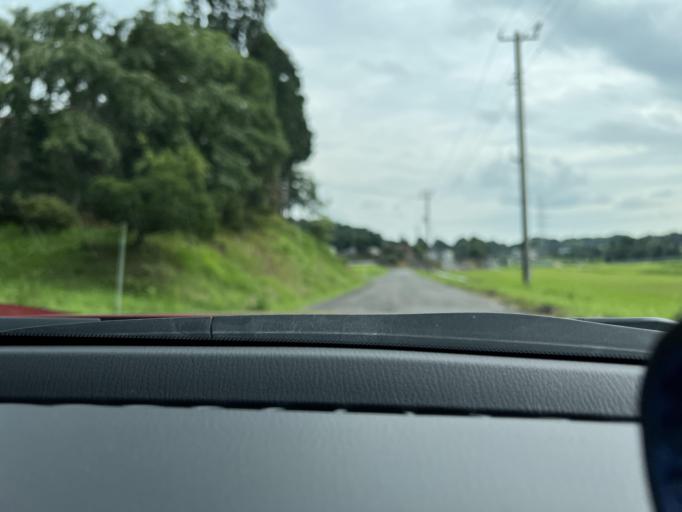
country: JP
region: Fukushima
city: Motomiya
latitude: 37.5139
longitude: 140.4327
